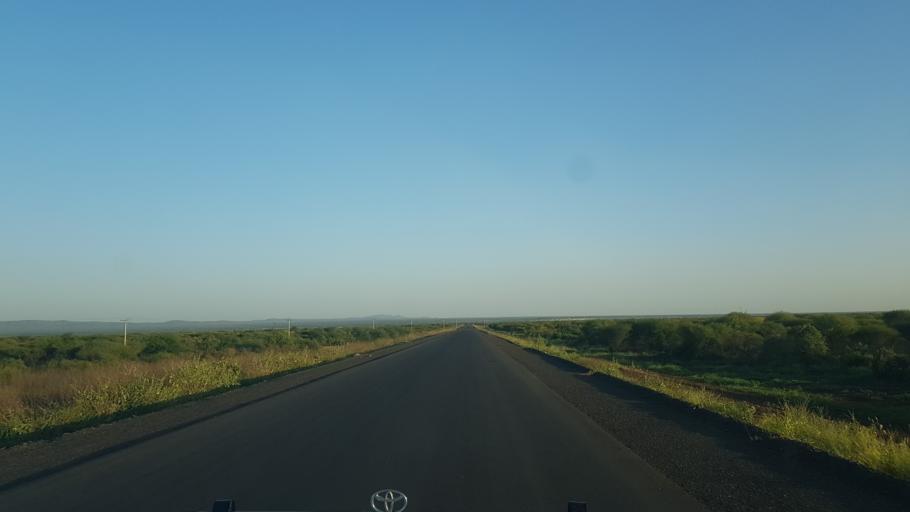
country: ET
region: Southern Nations, Nationalities, and People's Region
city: Lobuni
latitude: 5.1281
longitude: 36.1393
